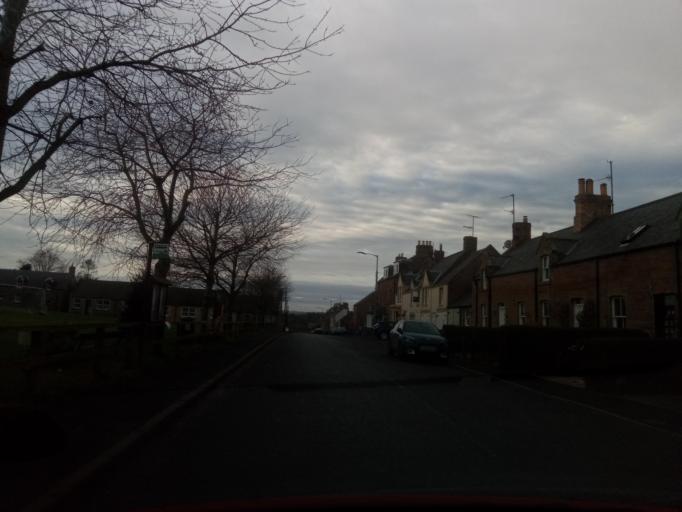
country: GB
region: Scotland
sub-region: The Scottish Borders
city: Coldstream
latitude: 55.7207
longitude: -2.2703
